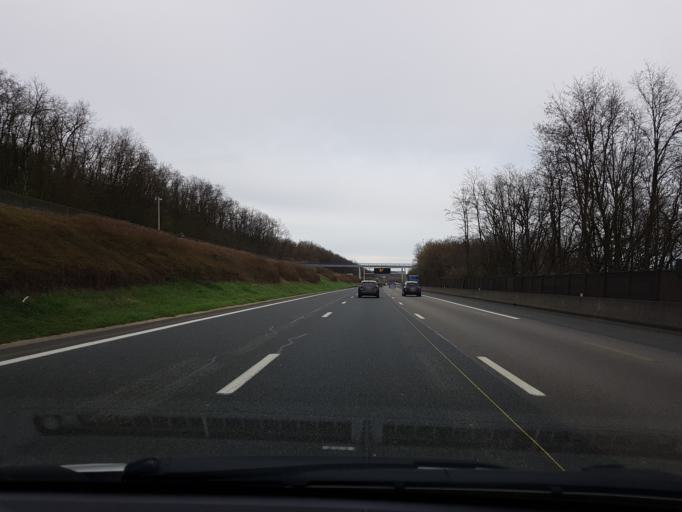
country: FR
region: Bourgogne
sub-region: Departement de Saone-et-Loire
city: Sance
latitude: 46.3431
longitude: 4.8230
